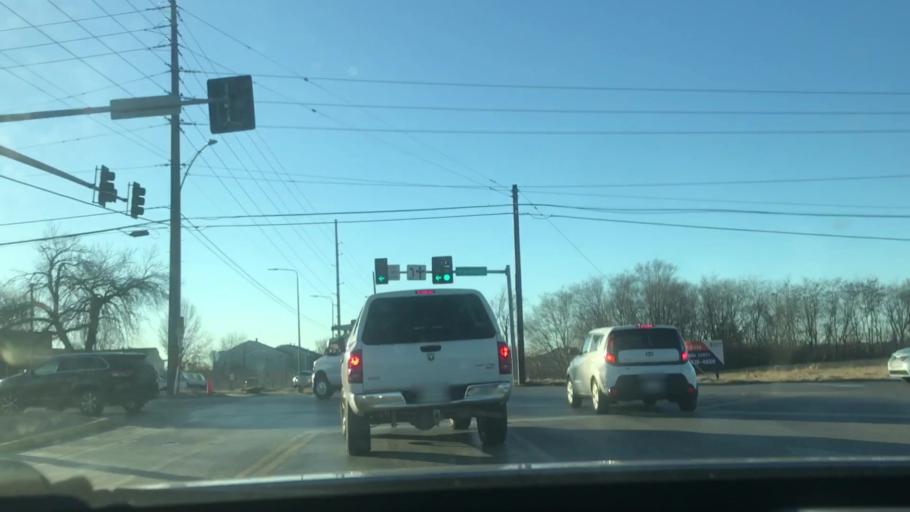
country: US
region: Missouri
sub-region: Clay County
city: Gladstone
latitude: 39.2247
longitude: -94.5851
